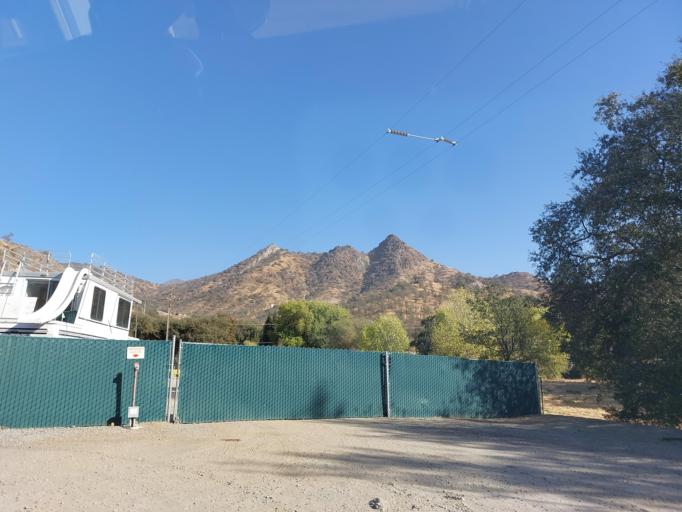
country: US
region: California
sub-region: Tulare County
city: Three Rivers
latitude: 36.4300
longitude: -118.9113
